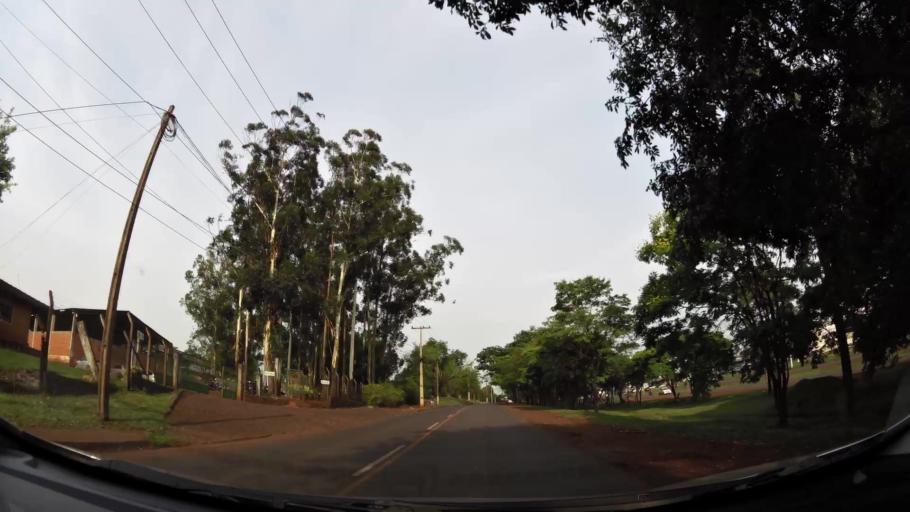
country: PY
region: Alto Parana
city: Ciudad del Este
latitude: -25.4967
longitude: -54.6697
